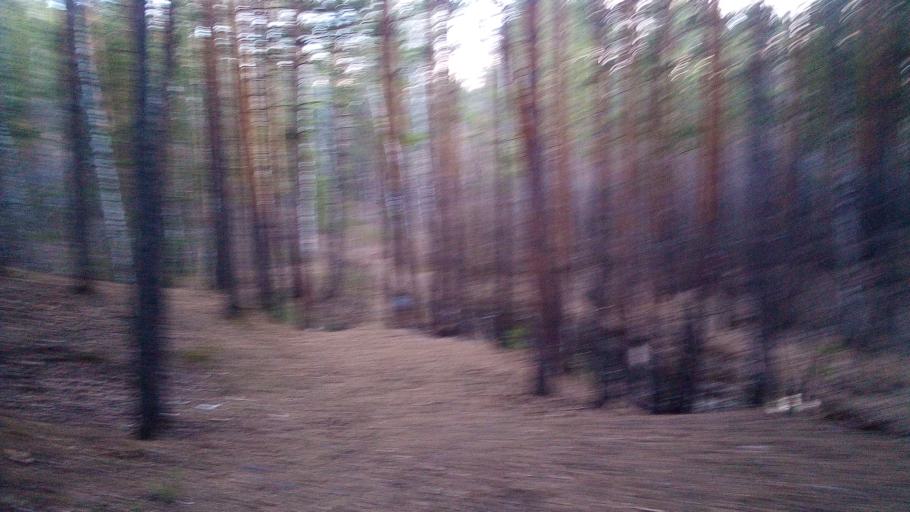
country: RU
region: Chelyabinsk
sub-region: Gorod Chelyabinsk
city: Chelyabinsk
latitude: 55.1655
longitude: 61.3263
